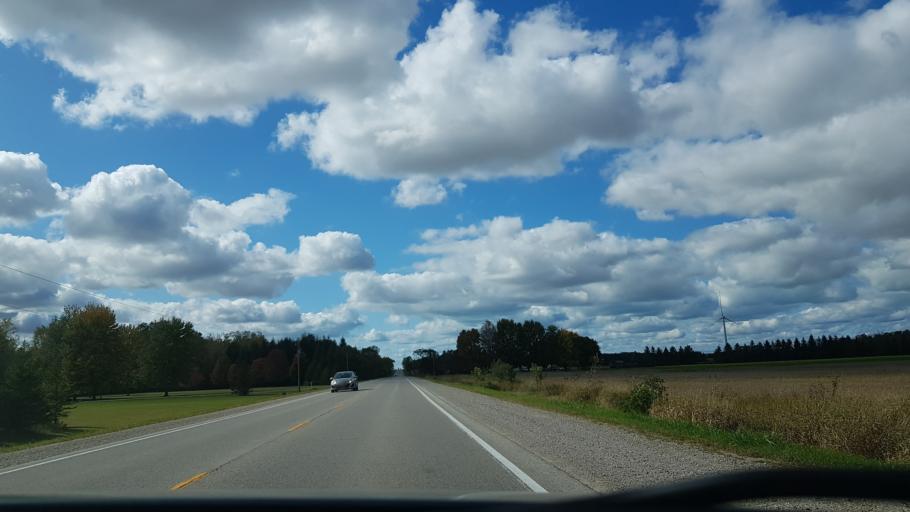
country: CA
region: Ontario
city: South Huron
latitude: 43.3537
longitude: -81.5604
